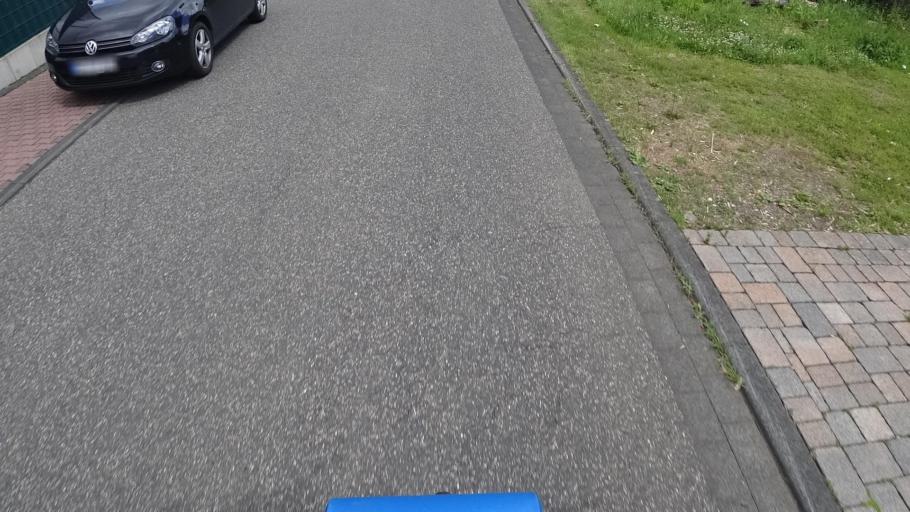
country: DE
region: Rheinland-Pfalz
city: Vettelschoss
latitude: 50.6194
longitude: 7.3239
